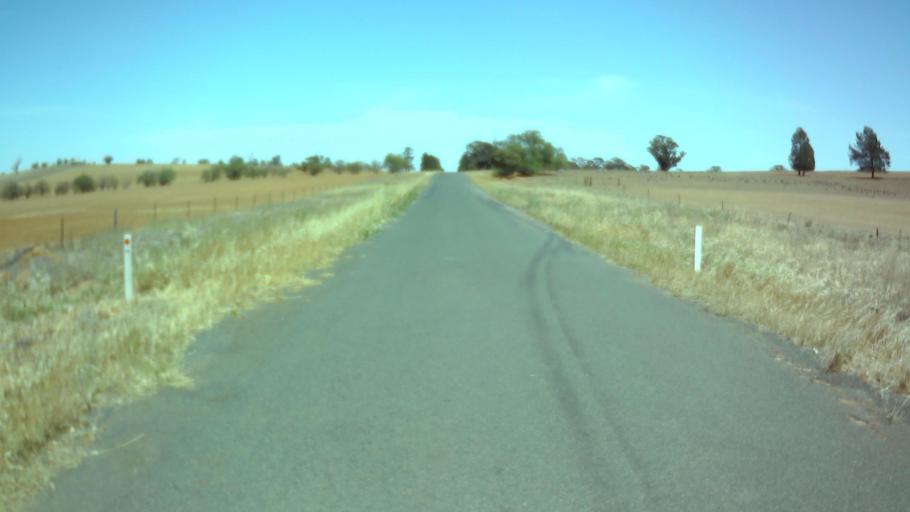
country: AU
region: New South Wales
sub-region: Weddin
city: Grenfell
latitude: -33.8564
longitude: 147.9478
